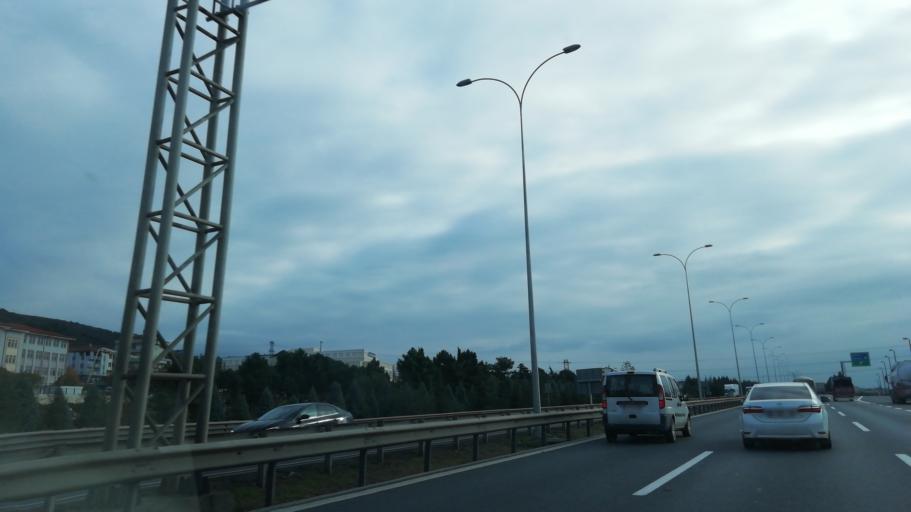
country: TR
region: Kocaeli
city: Korfez
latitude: 40.7736
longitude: 29.7649
